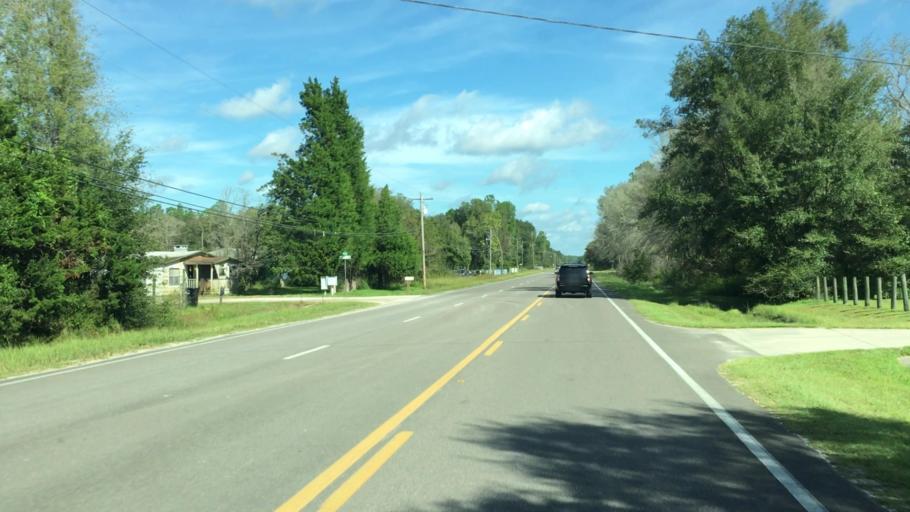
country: US
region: Florida
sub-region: Alachua County
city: Gainesville
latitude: 29.7190
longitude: -82.2771
